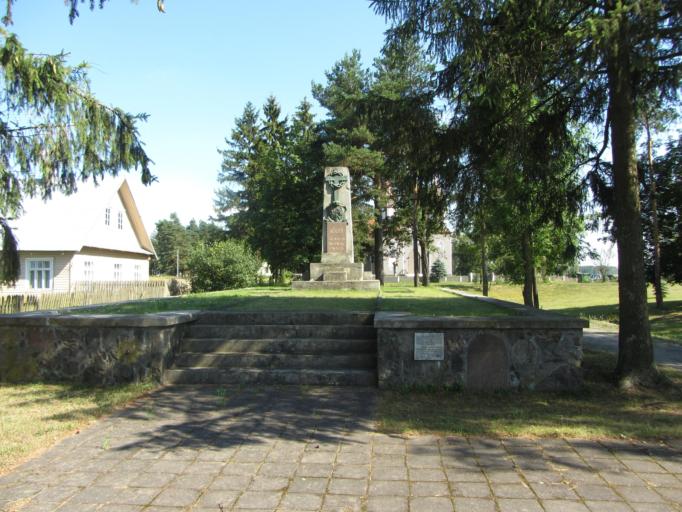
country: LT
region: Alytaus apskritis
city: Varena
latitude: 54.0190
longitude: 24.7468
